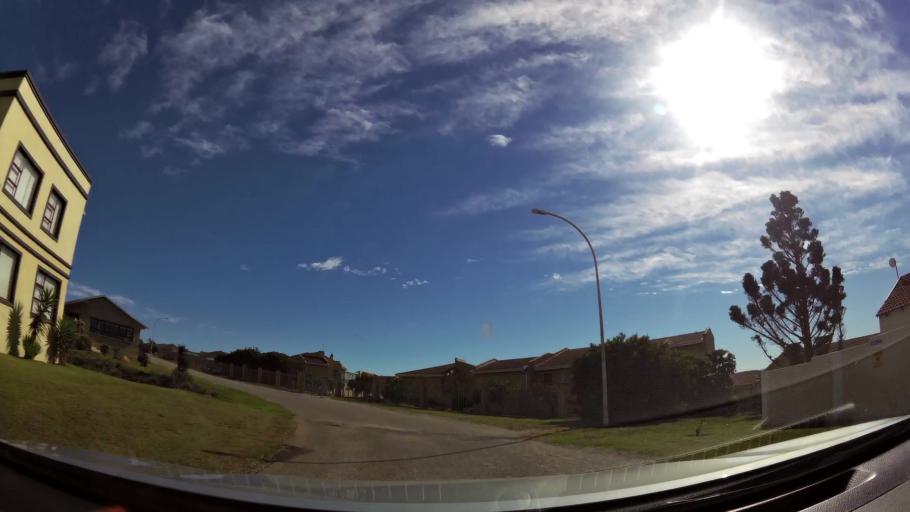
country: ZA
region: Eastern Cape
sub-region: Cacadu District Municipality
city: Jeffrey's Bay
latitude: -34.0143
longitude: 24.9226
